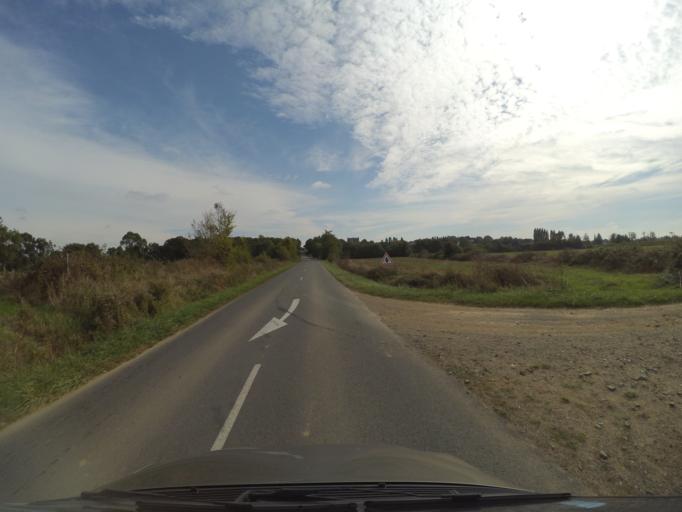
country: FR
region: Pays de la Loire
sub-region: Departement de Maine-et-Loire
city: Saint-Jean
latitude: 47.2023
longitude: -0.3794
